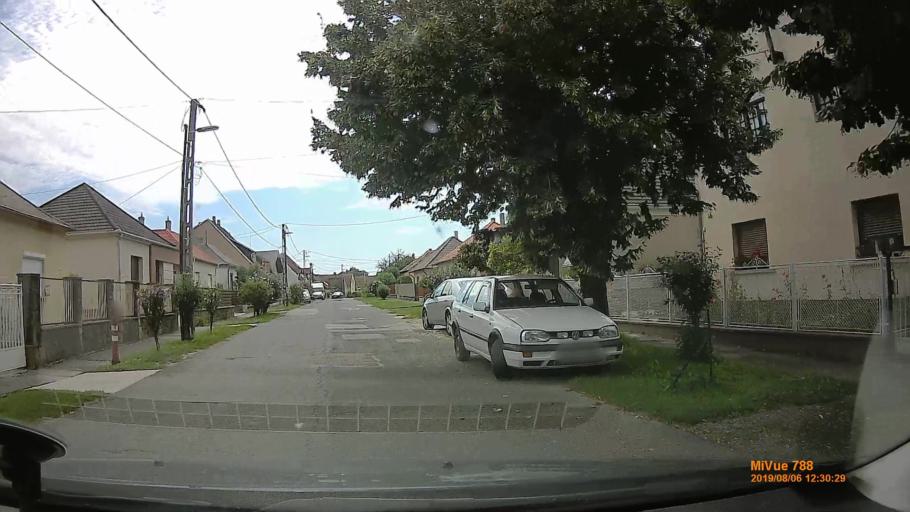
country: HU
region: Zala
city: Nagykanizsa
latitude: 46.4654
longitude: 16.9884
